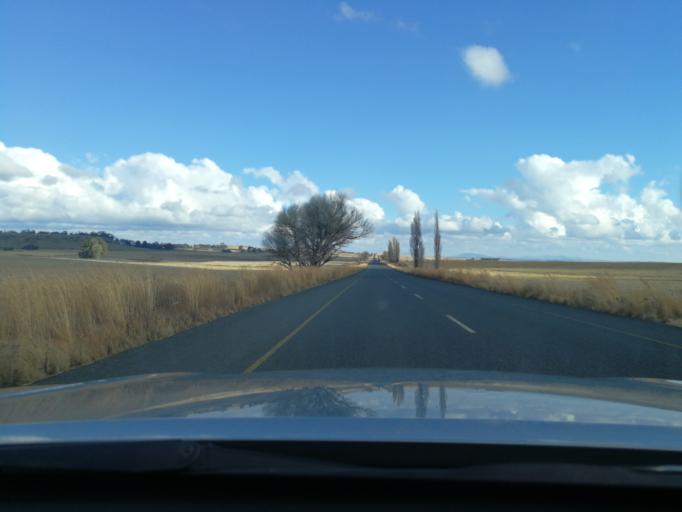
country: ZA
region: Orange Free State
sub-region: Thabo Mofutsanyana District Municipality
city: Bethlehem
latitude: -28.0260
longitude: 28.3734
